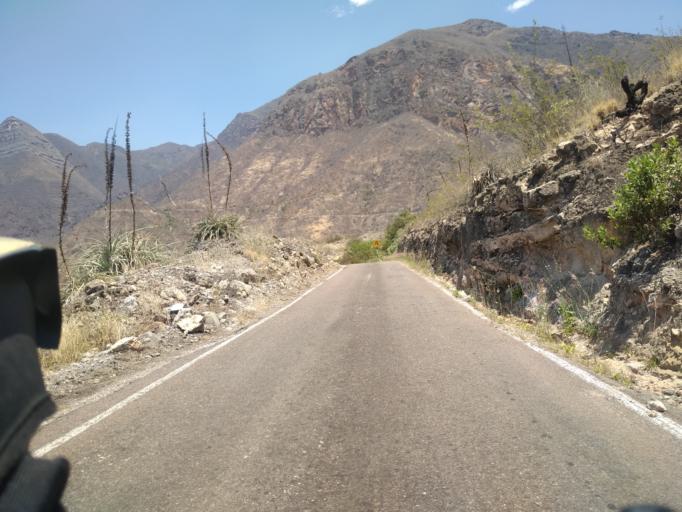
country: PE
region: Amazonas
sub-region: Provincia de Chachapoyas
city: Balsas
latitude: -6.8475
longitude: -78.0437
